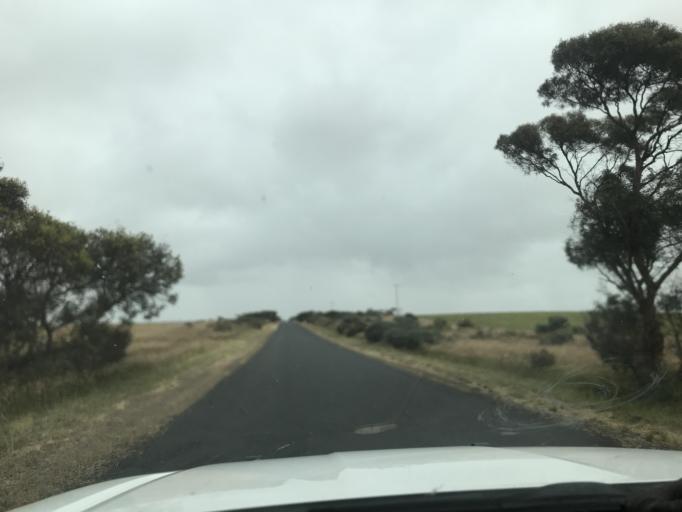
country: AU
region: South Australia
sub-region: Tatiara
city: Bordertown
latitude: -36.1175
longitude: 141.0405
